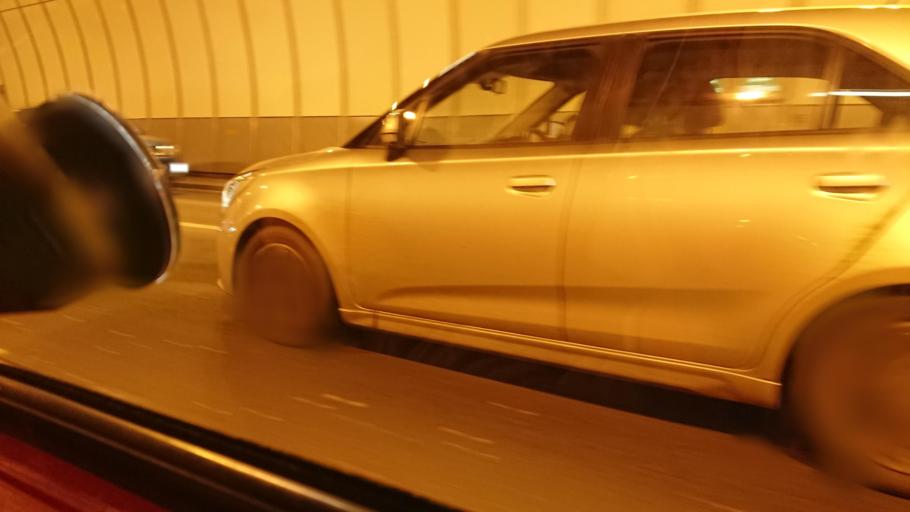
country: GB
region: England
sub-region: Cornwall
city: Saltash
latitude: 50.4104
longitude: -4.2134
